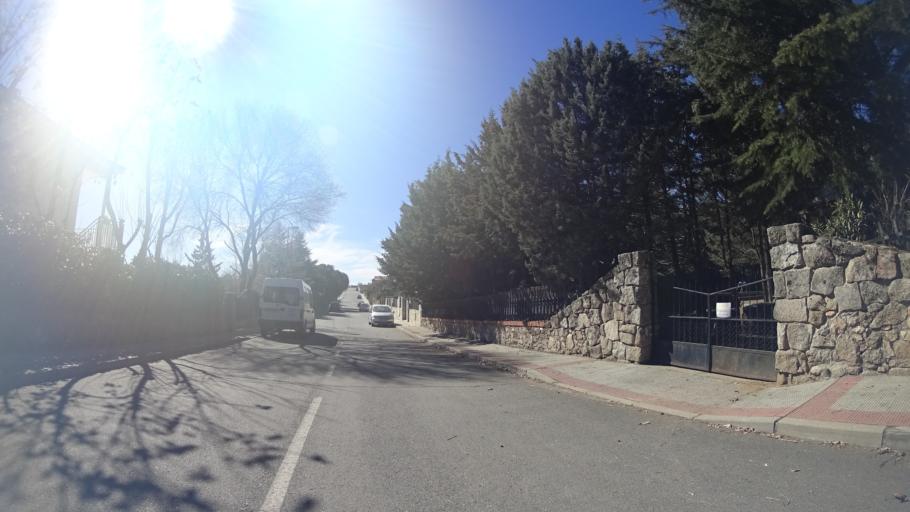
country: ES
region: Madrid
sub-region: Provincia de Madrid
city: Colmenarejo
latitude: 40.5512
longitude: -4.0046
